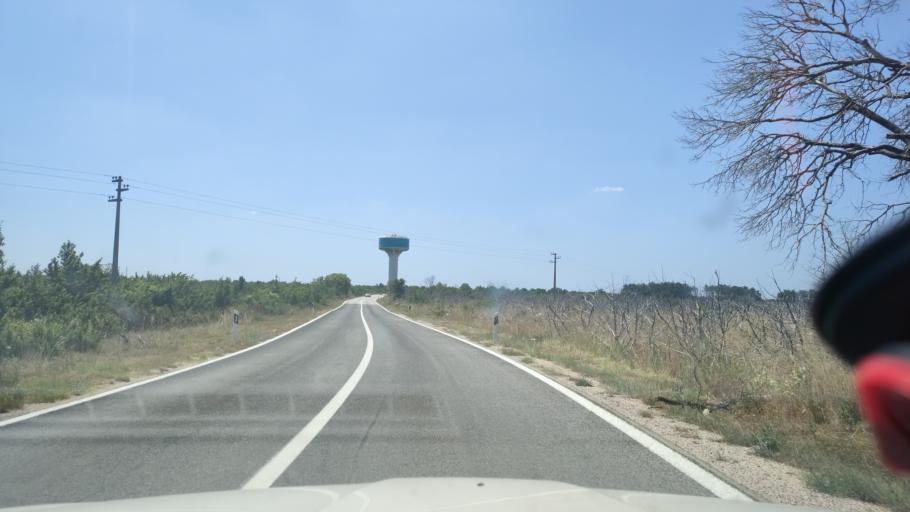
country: HR
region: Sibensko-Kniniska
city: Kistanje
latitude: 43.9978
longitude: 15.9830
